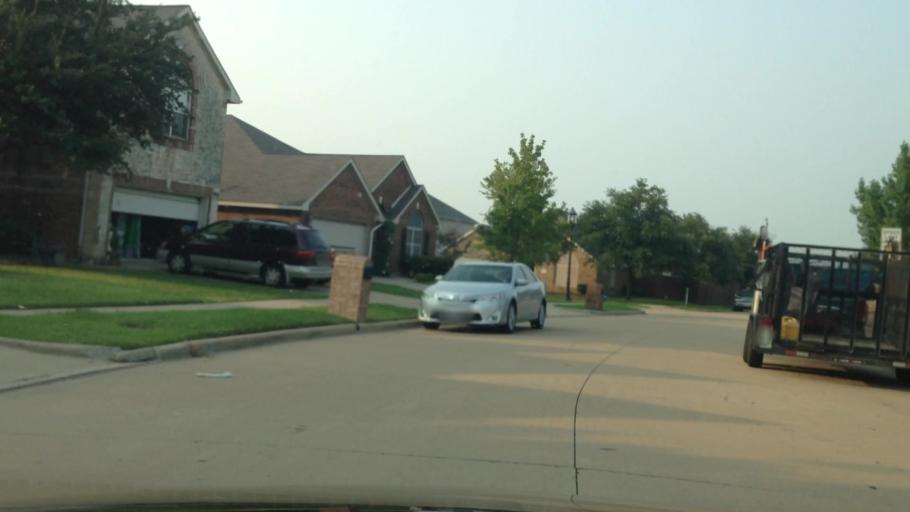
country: US
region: Texas
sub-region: Collin County
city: Frisco
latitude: 33.1317
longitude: -96.8362
